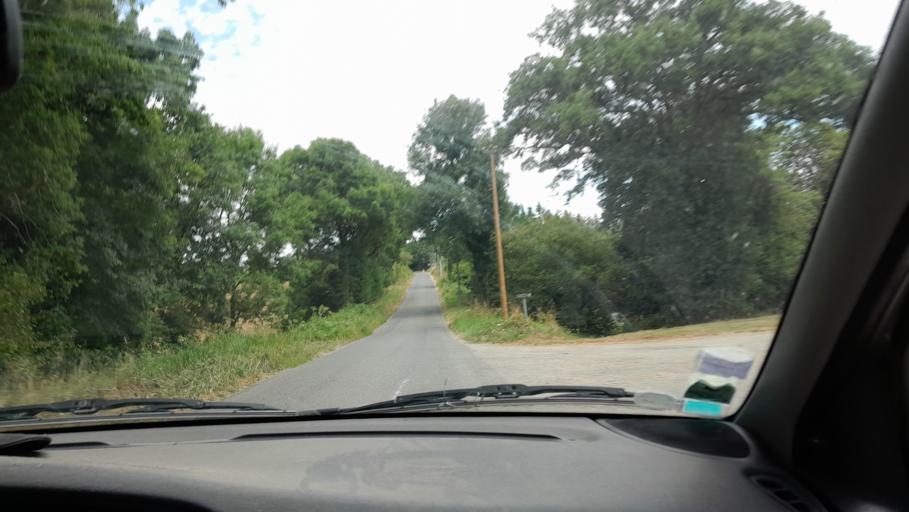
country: FR
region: Pays de la Loire
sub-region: Departement de la Mayenne
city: Juvigne
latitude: 48.1839
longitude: -1.0357
